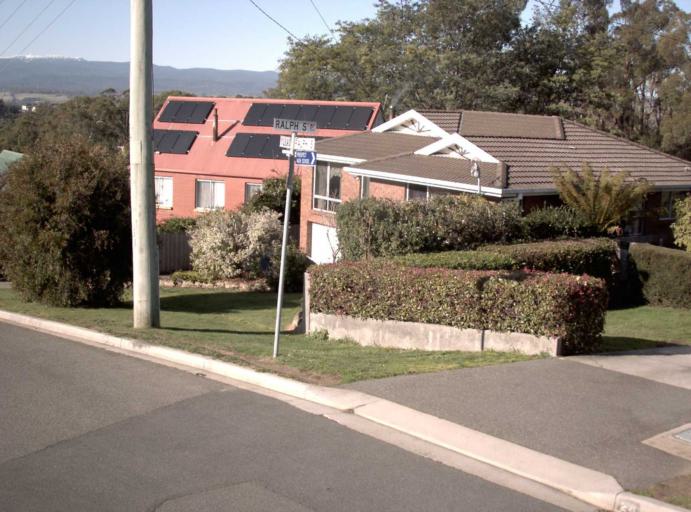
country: AU
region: Tasmania
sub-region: Launceston
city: Summerhill
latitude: -41.4745
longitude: 147.1325
